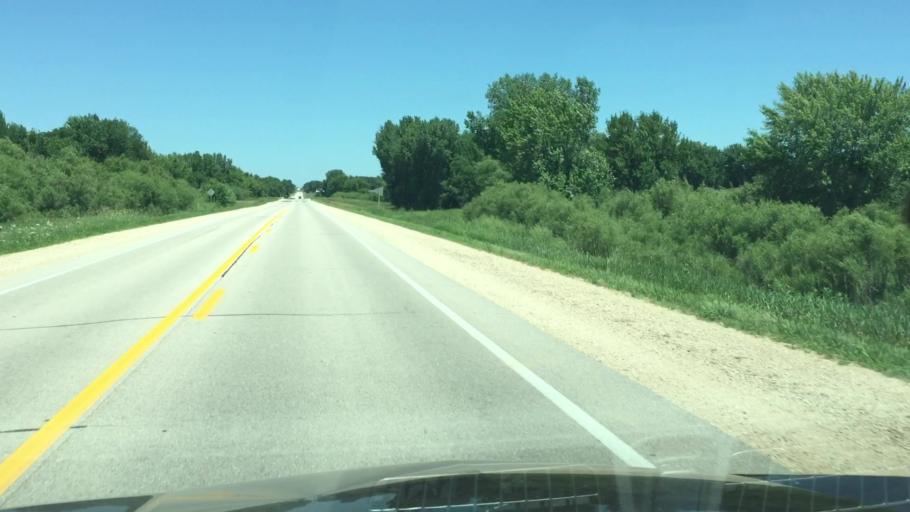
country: US
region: Iowa
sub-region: Cedar County
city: Mechanicsville
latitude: 42.0133
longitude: -91.1368
